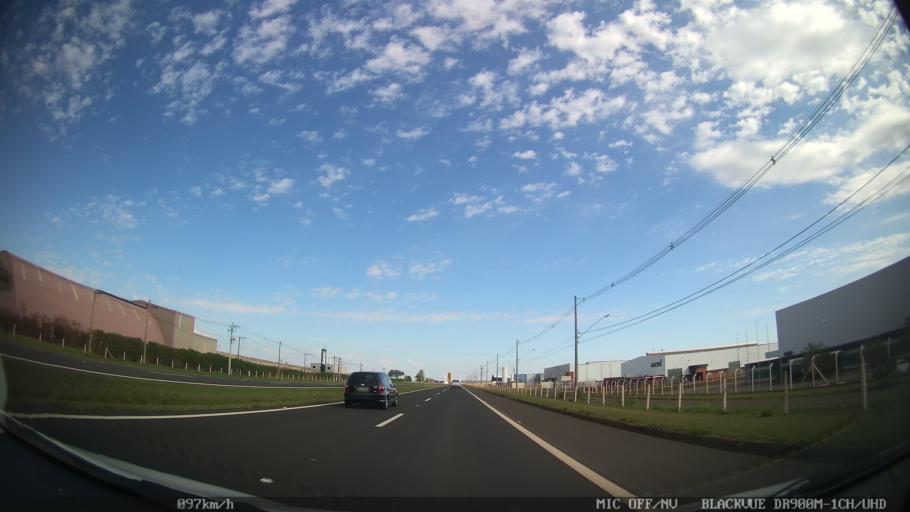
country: BR
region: Sao Paulo
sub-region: Iracemapolis
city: Iracemapolis
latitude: -22.6108
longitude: -47.4779
